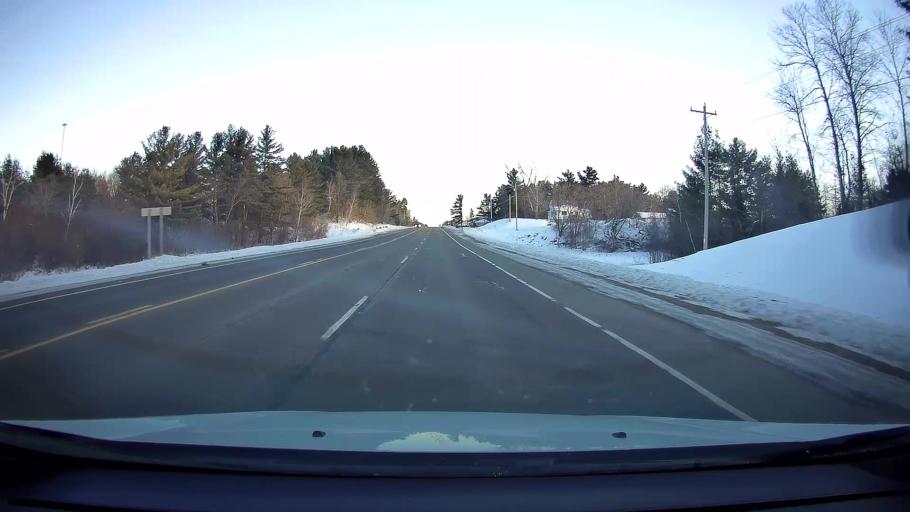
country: US
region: Wisconsin
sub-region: Barron County
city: Cumberland
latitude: 45.5689
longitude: -92.0174
